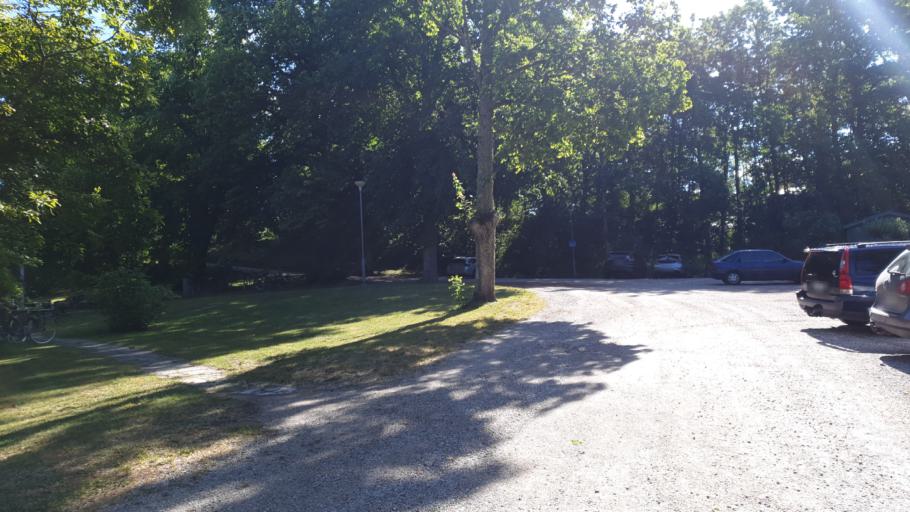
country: SE
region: Gotland
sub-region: Gotland
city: Vibble
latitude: 57.5999
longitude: 18.2164
